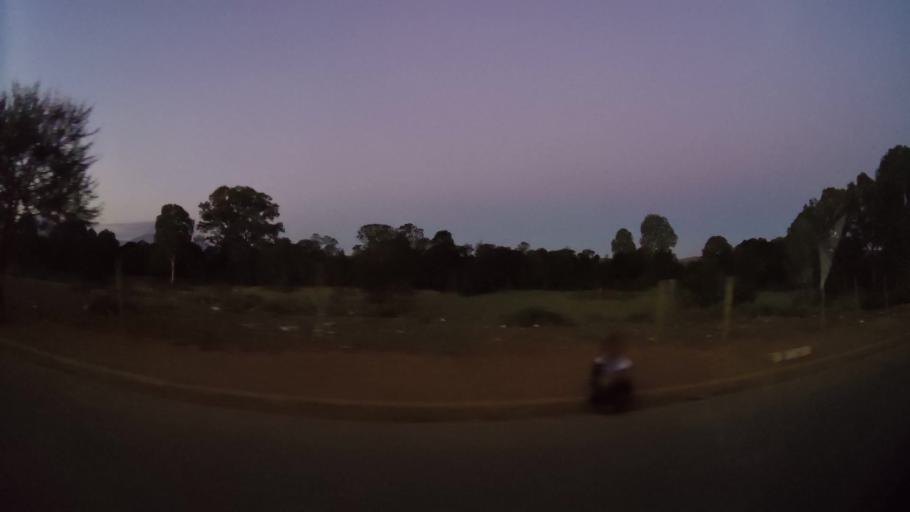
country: ZA
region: Western Cape
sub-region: Eden District Municipality
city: Riversdale
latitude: -34.1053
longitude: 21.2746
